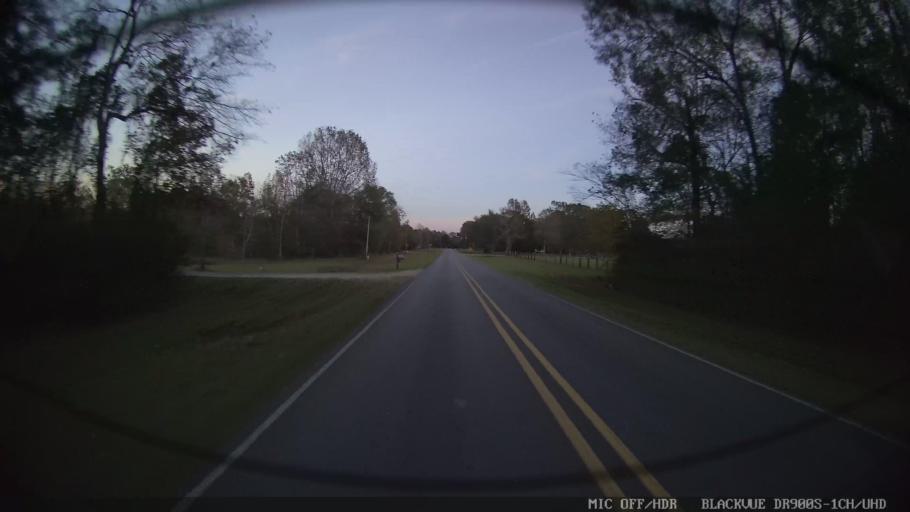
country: US
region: Mississippi
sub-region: Perry County
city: New Augusta
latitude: 31.0708
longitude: -89.1989
